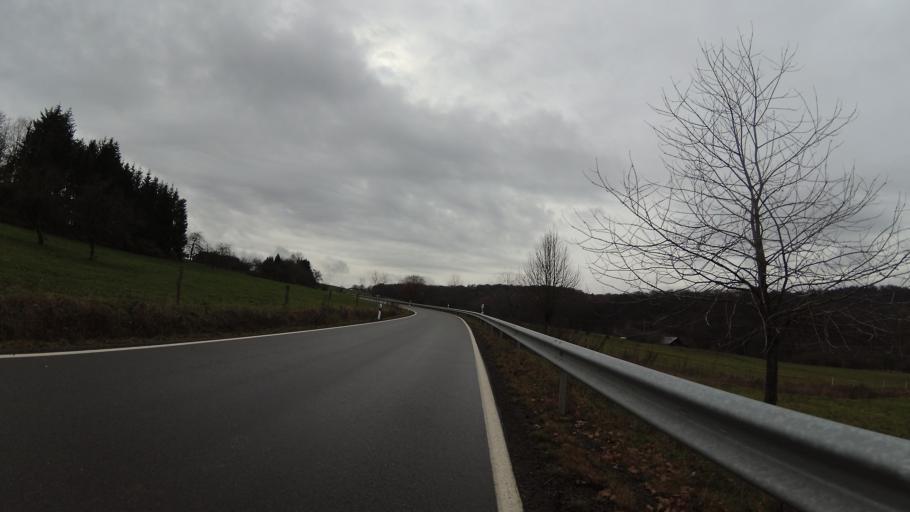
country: DE
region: Rheinland-Pfalz
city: Frohnhofen
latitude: 49.4496
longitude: 7.2978
